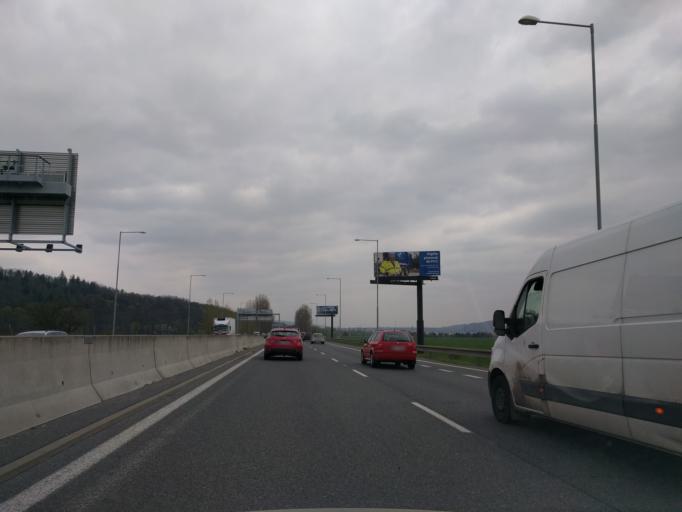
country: CZ
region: Praha
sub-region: Praha 12
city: Modrany
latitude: 49.9815
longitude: 14.3893
